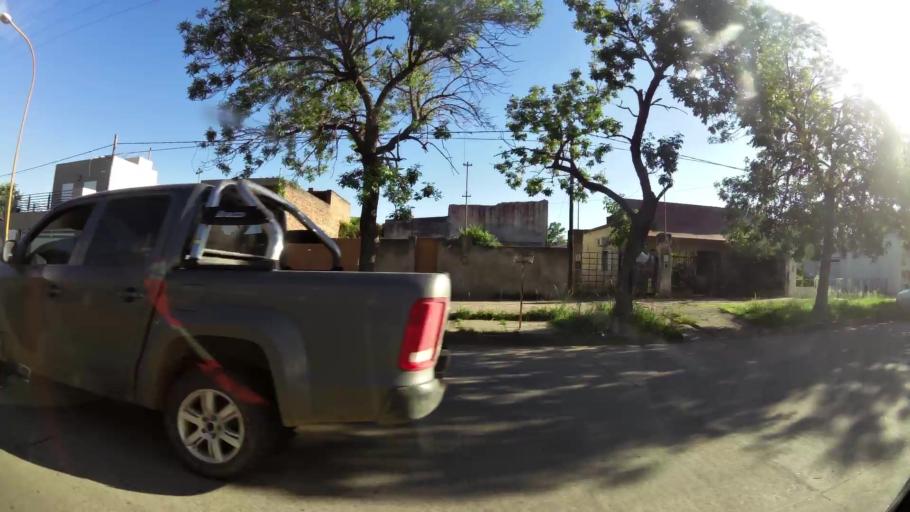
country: AR
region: Cordoba
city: San Francisco
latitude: -31.4379
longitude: -62.0719
